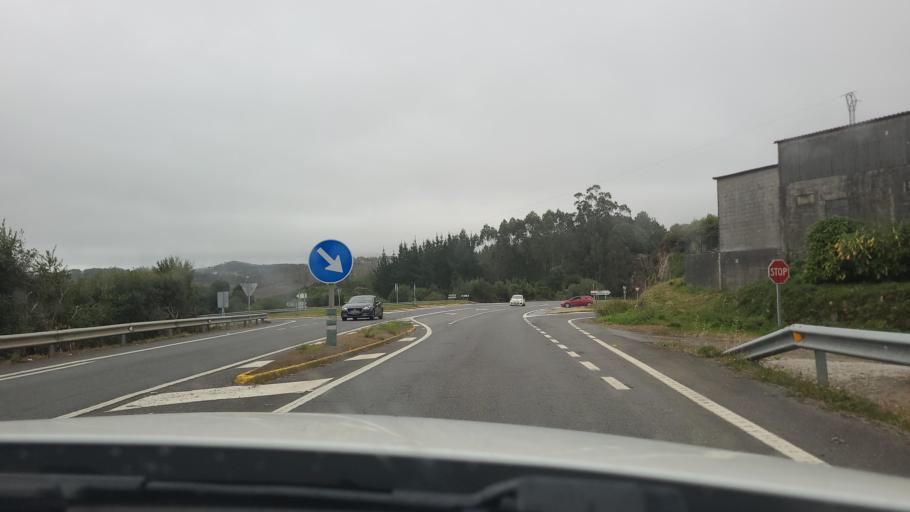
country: ES
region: Galicia
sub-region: Provincia da Coruna
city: Dumbria
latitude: 43.0580
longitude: -9.0861
